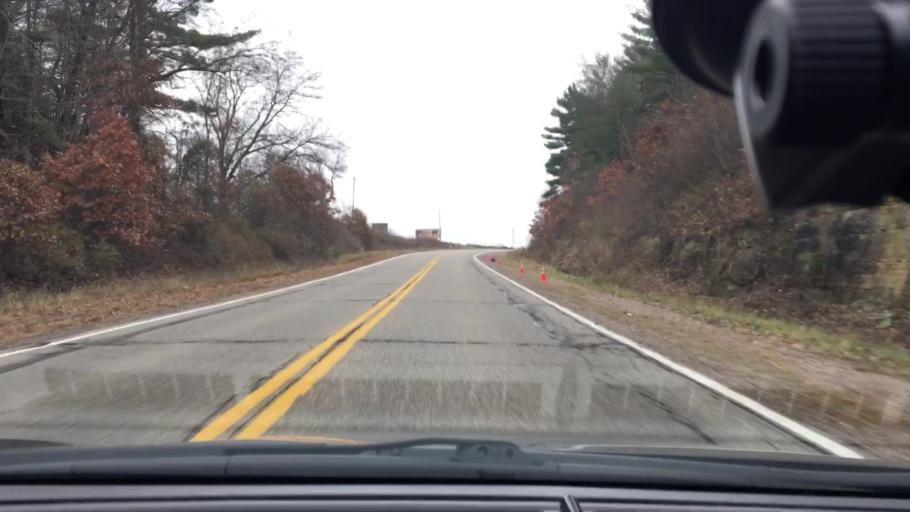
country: US
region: Wisconsin
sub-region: Columbia County
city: Wisconsin Dells
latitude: 43.6397
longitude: -89.7992
